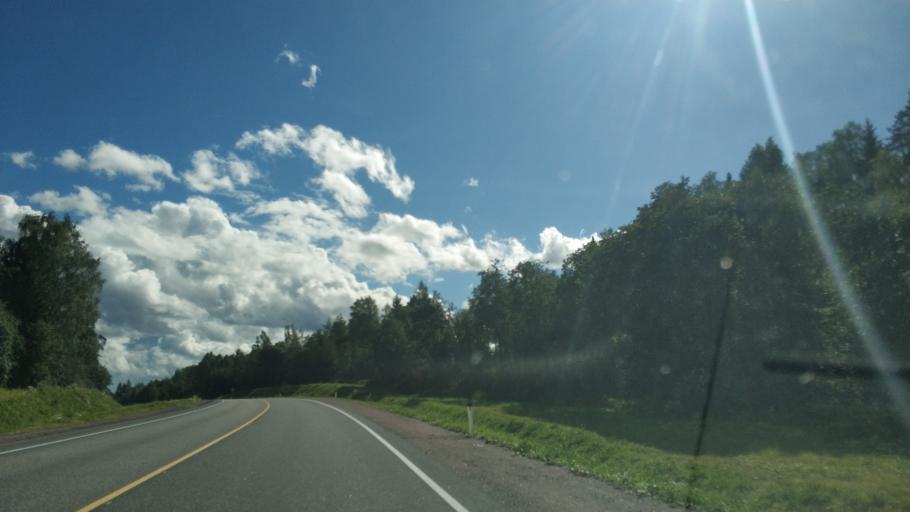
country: RU
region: Republic of Karelia
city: Ruskeala
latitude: 61.8968
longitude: 30.6369
